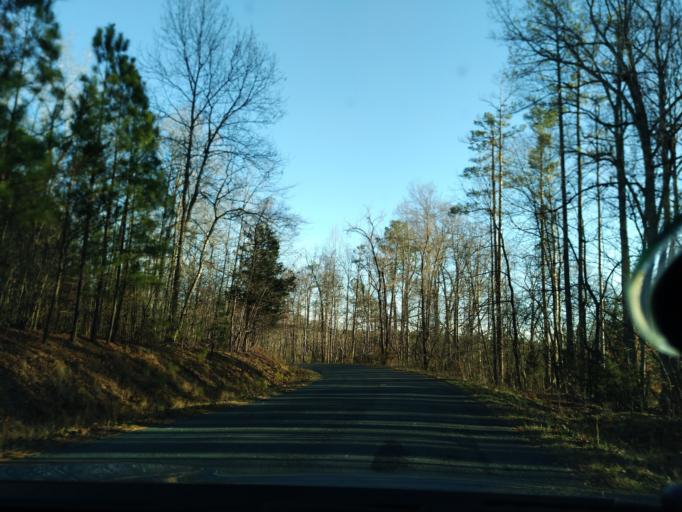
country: US
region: Virginia
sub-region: Appomattox County
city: Appomattox
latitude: 37.3838
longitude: -78.6514
